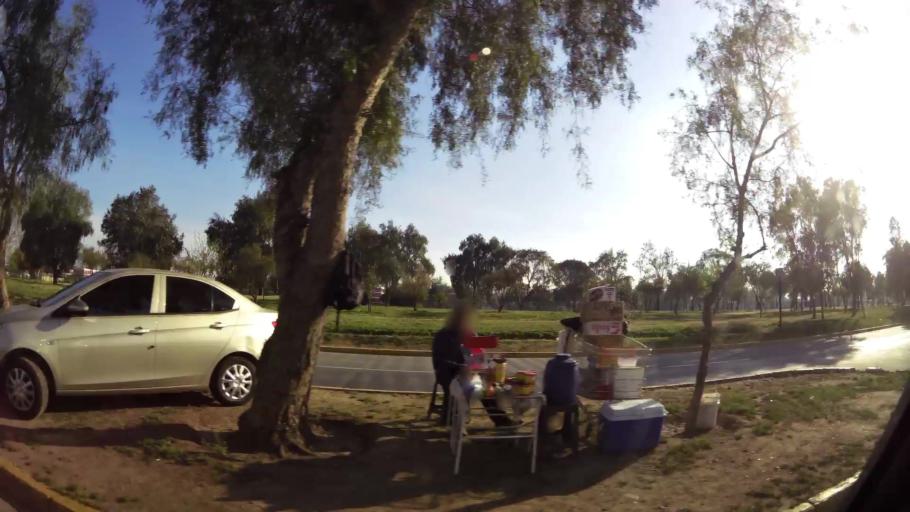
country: CL
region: Santiago Metropolitan
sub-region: Provincia de Santiago
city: Lo Prado
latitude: -33.4538
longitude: -70.7416
